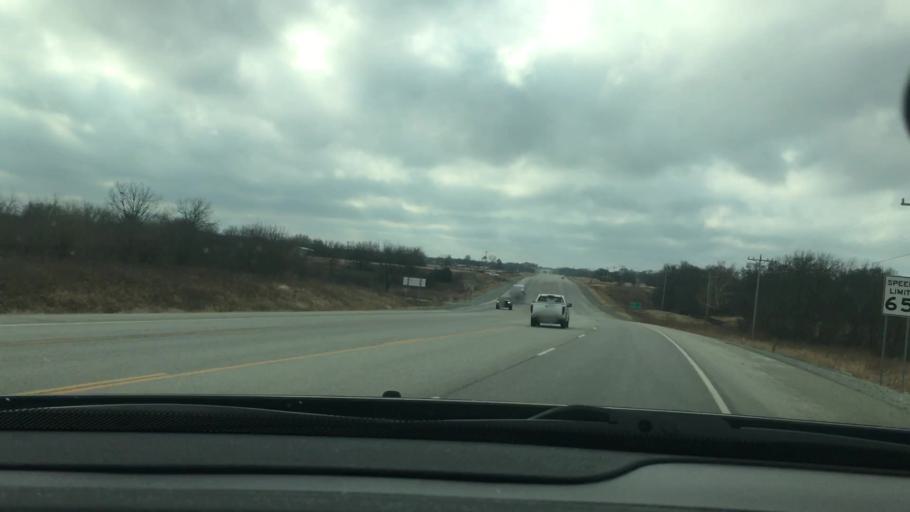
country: US
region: Oklahoma
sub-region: Bryan County
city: Durant
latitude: 34.0804
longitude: -96.3730
